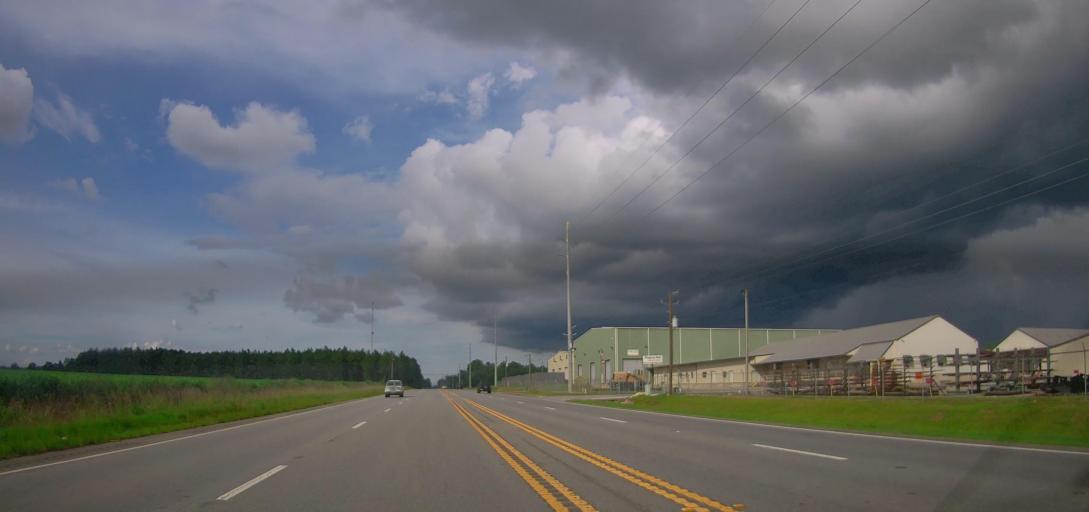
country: US
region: Georgia
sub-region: Pierce County
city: Blackshear
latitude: 31.3995
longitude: -82.1249
